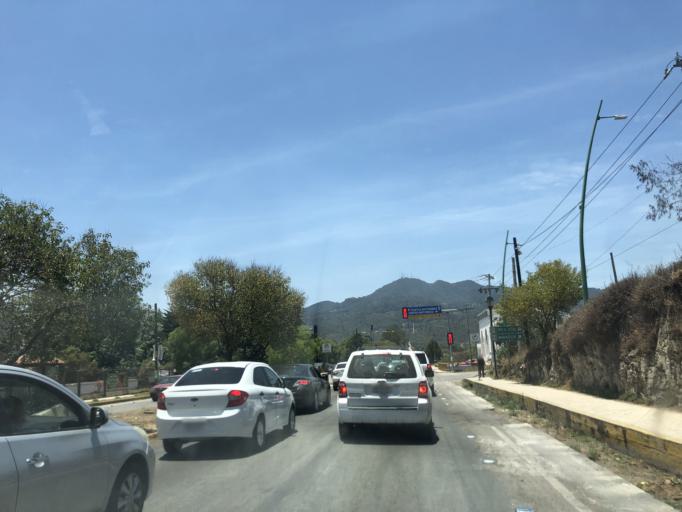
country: MX
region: Chiapas
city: San Cristobal de las Casas
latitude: 16.7319
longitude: -92.6486
